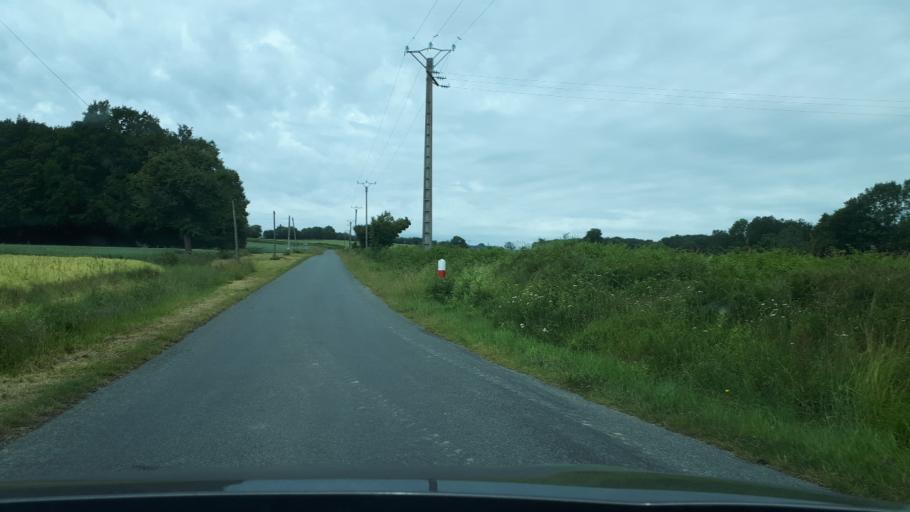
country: FR
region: Centre
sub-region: Departement du Cher
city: Blancafort
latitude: 47.4172
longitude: 2.6212
